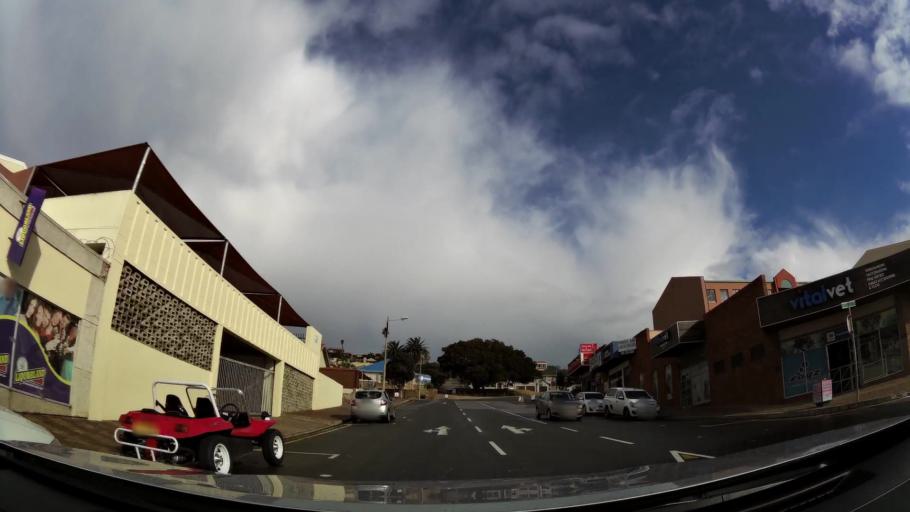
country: ZA
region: Western Cape
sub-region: Eden District Municipality
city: Mossel Bay
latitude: -34.1831
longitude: 22.1428
